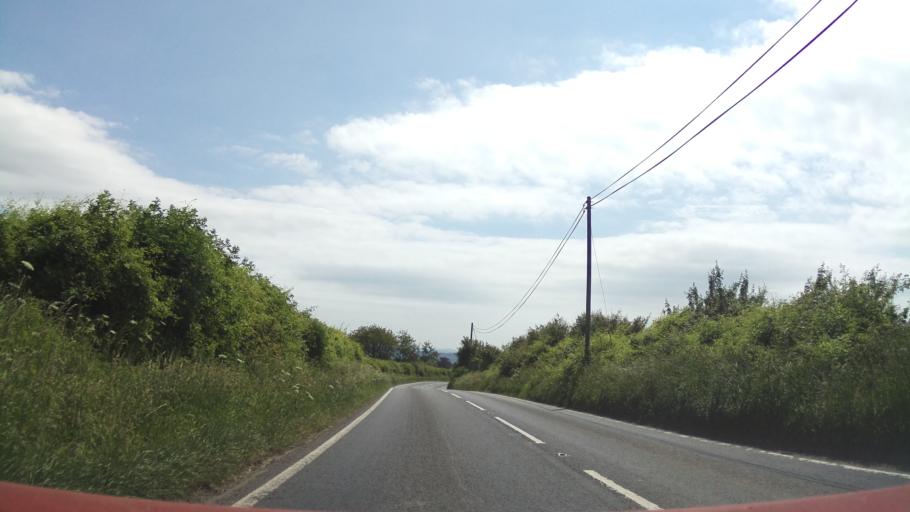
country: GB
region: England
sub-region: Somerset
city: Wincanton
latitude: 51.0578
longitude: -2.4541
